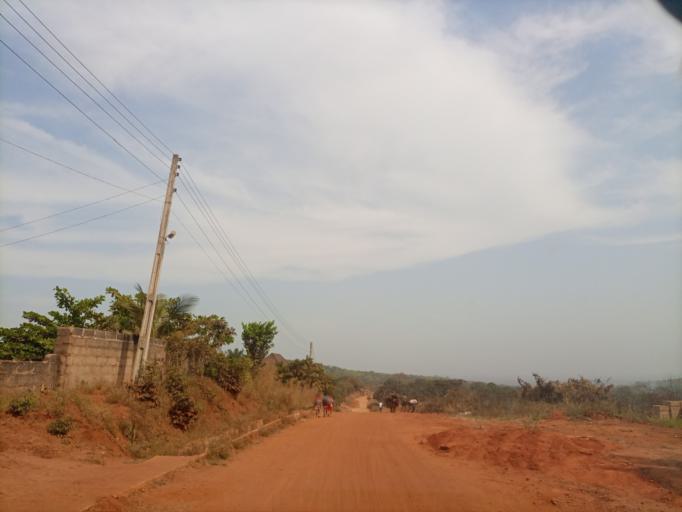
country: NG
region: Enugu
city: Opi
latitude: 6.8220
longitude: 7.4761
